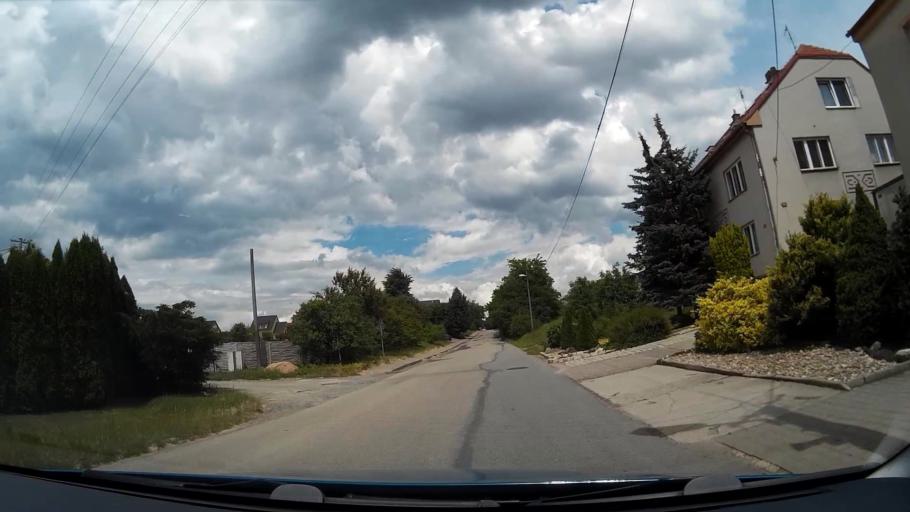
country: CZ
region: South Moravian
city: Orechov
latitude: 49.1128
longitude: 16.5254
